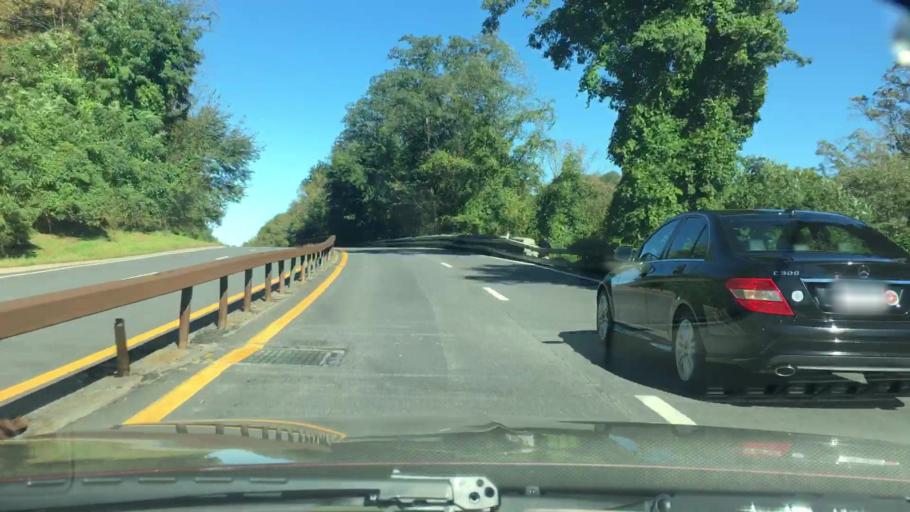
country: US
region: New York
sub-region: Westchester County
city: Pleasantville
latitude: 41.1467
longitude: -73.7860
